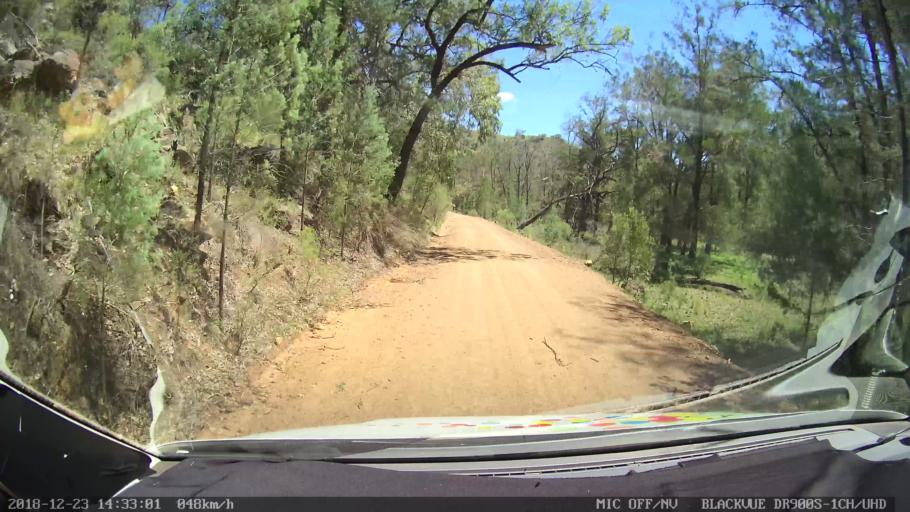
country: AU
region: New South Wales
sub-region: Tamworth Municipality
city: Manilla
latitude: -30.6056
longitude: 150.9152
